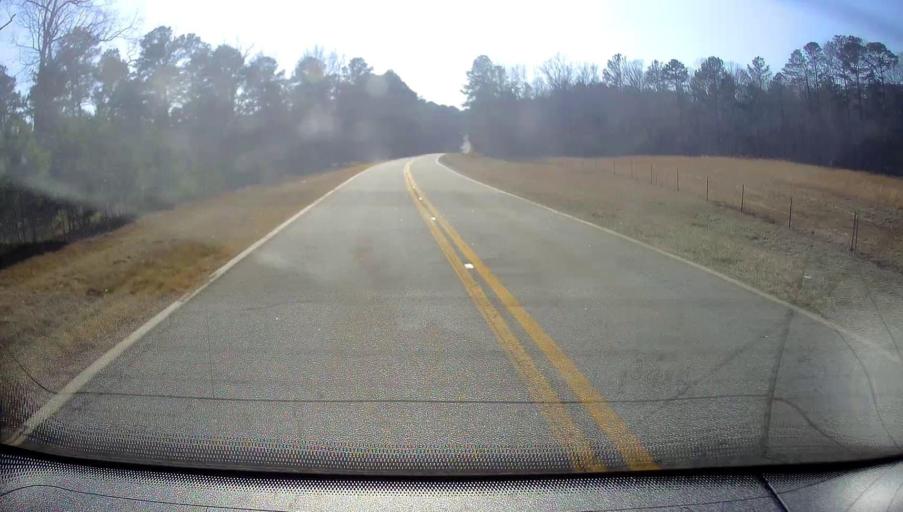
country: US
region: Georgia
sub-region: Monroe County
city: Forsyth
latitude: 33.0847
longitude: -83.8434
